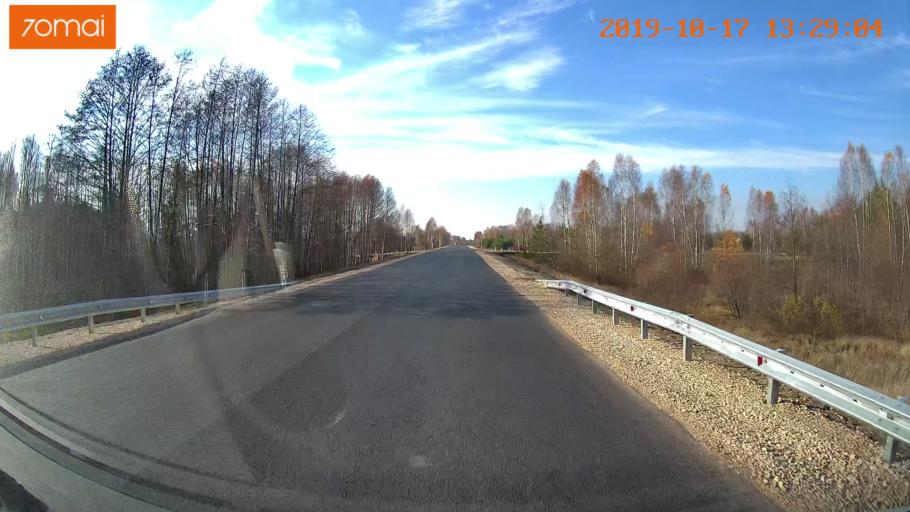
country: RU
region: Vladimir
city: Velikodvorskiy
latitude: 55.1182
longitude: 40.8511
